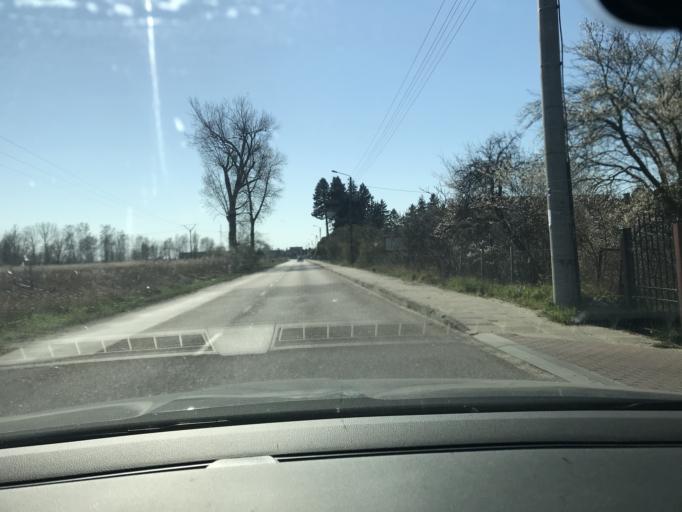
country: PL
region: Pomeranian Voivodeship
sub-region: Powiat nowodworski
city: Sztutowo
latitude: 54.3431
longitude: 19.2428
